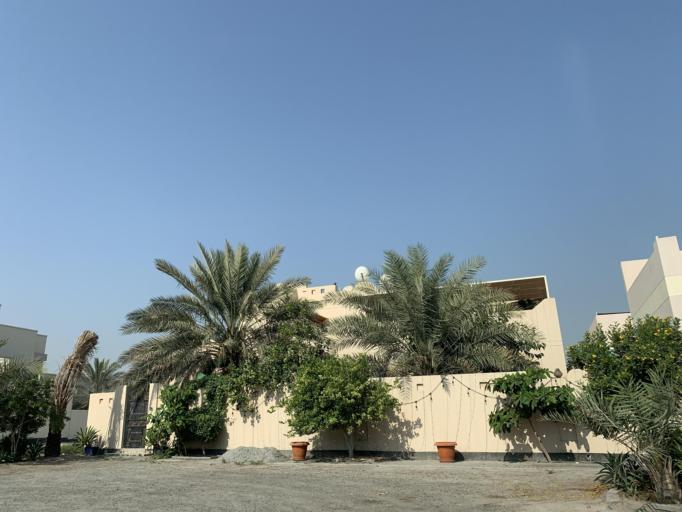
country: BH
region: Manama
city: Jidd Hafs
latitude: 26.1975
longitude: 50.5131
